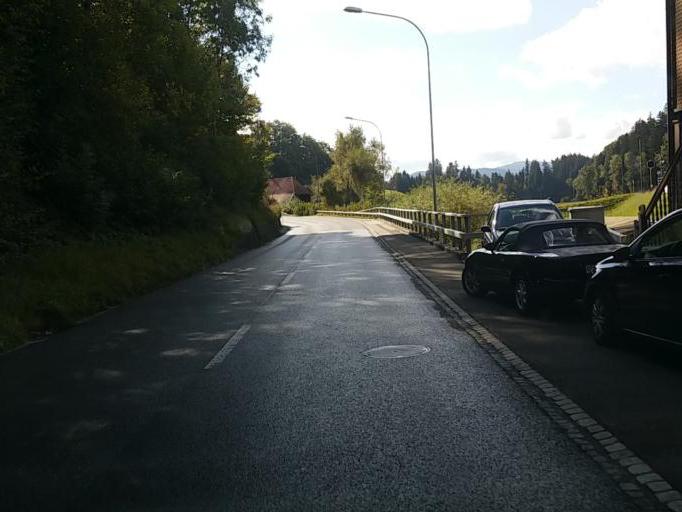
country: CH
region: Bern
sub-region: Emmental District
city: Sumiswald
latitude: 47.0351
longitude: 7.7383
